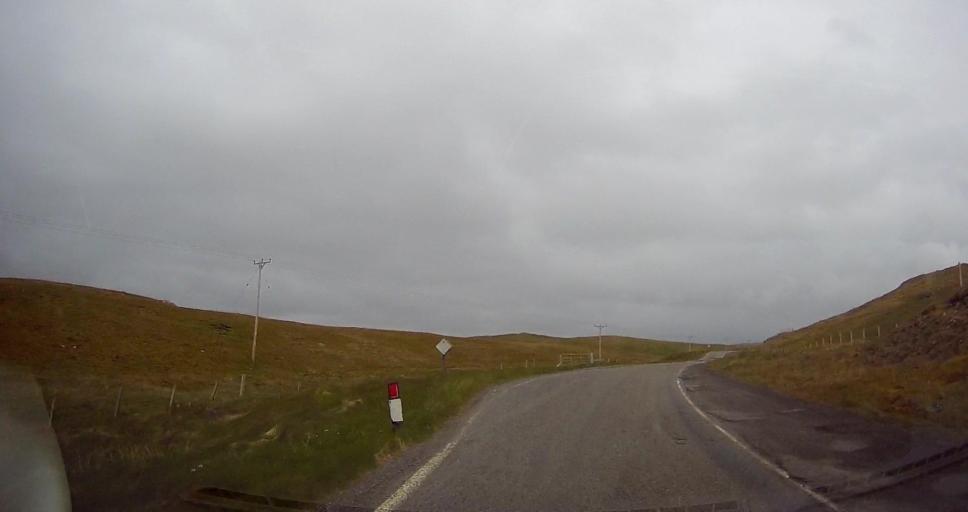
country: GB
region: Scotland
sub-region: Shetland Islands
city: Sandwick
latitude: 60.2354
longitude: -1.5483
